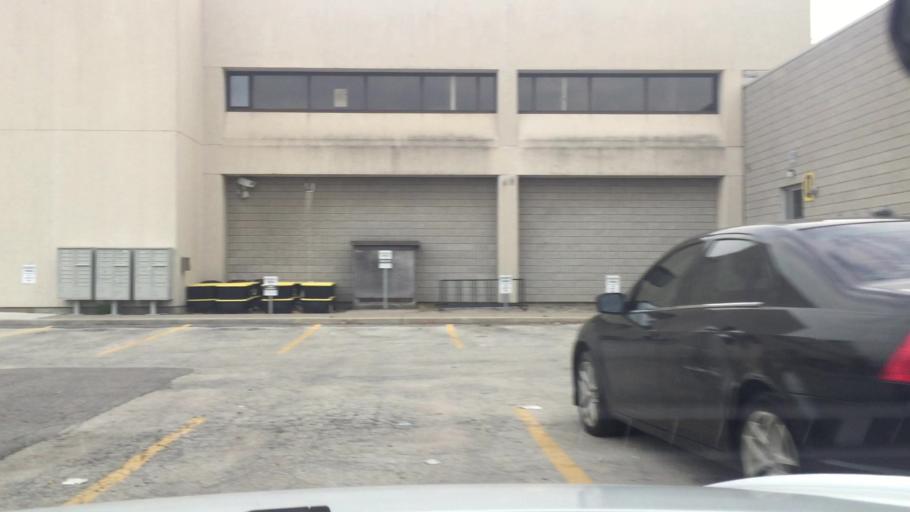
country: CA
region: Ontario
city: Scarborough
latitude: 43.7114
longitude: -79.3132
